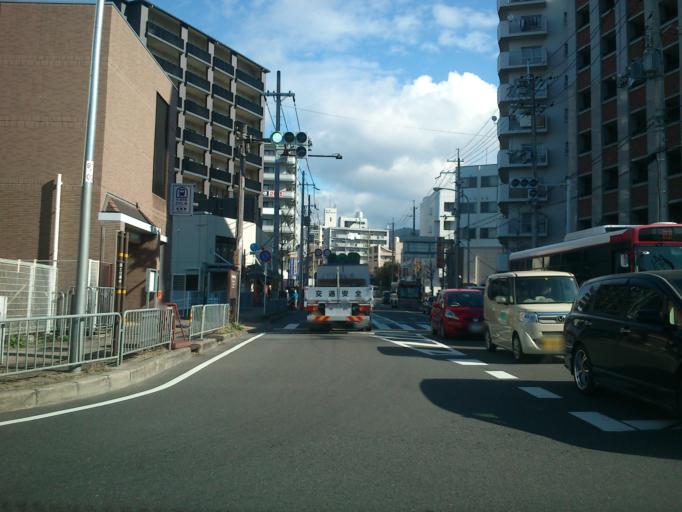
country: JP
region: Shiga Prefecture
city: Otsu-shi
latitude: 34.9813
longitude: 135.8164
